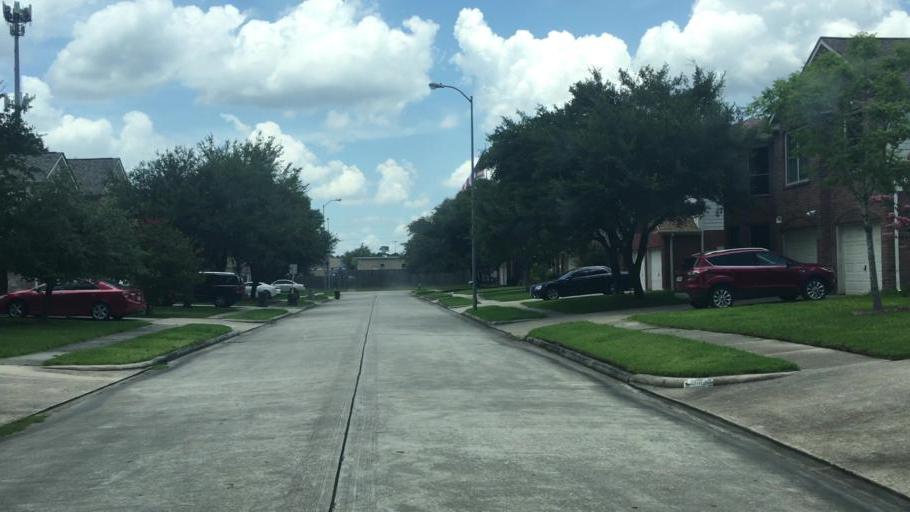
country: US
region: Texas
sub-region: Harris County
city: Atascocita
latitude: 29.9929
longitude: -95.1746
